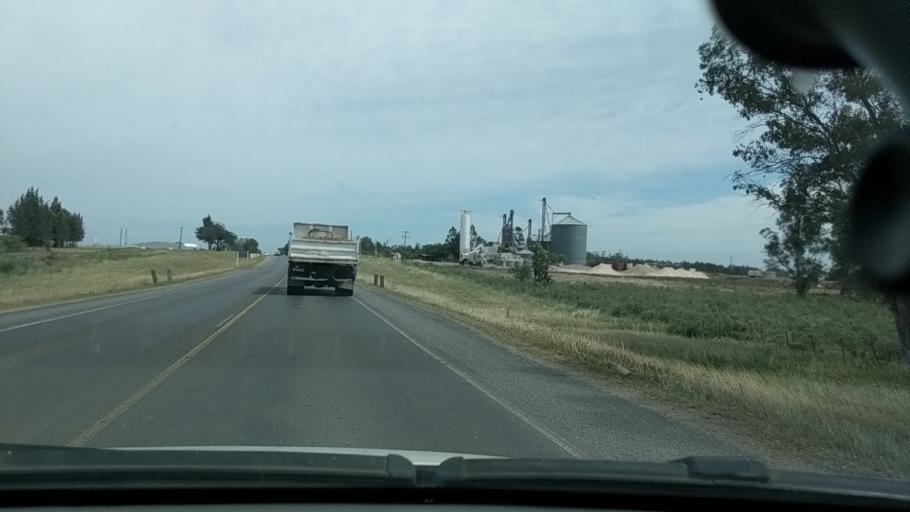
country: UY
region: Durazno
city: Durazno
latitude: -33.4249
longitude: -56.4997
